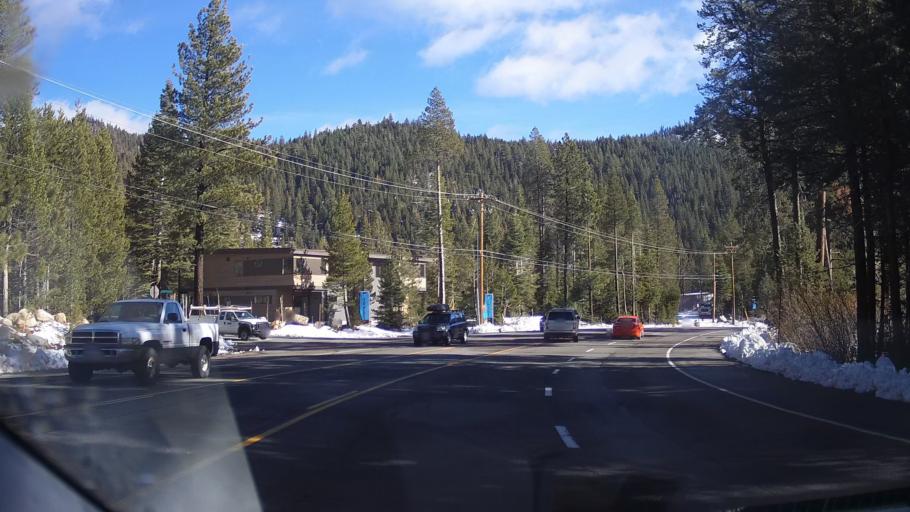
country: US
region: California
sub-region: Placer County
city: Sunnyside-Tahoe City
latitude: 39.2060
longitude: -120.2036
